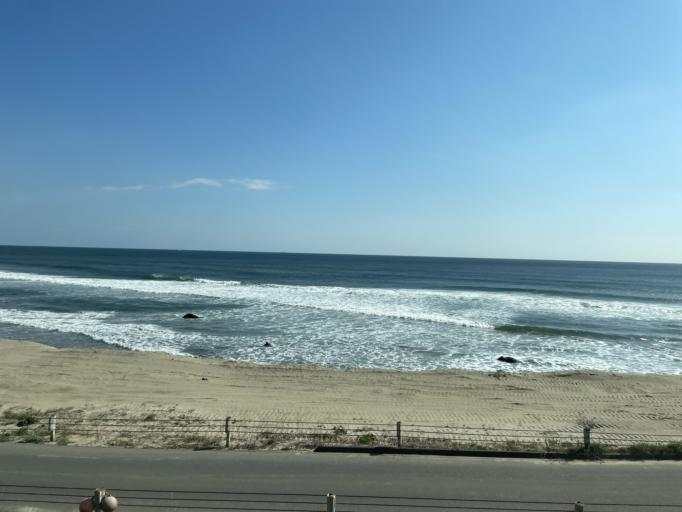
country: JP
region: Aomori
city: Hachinohe
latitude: 40.3211
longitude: 141.7739
